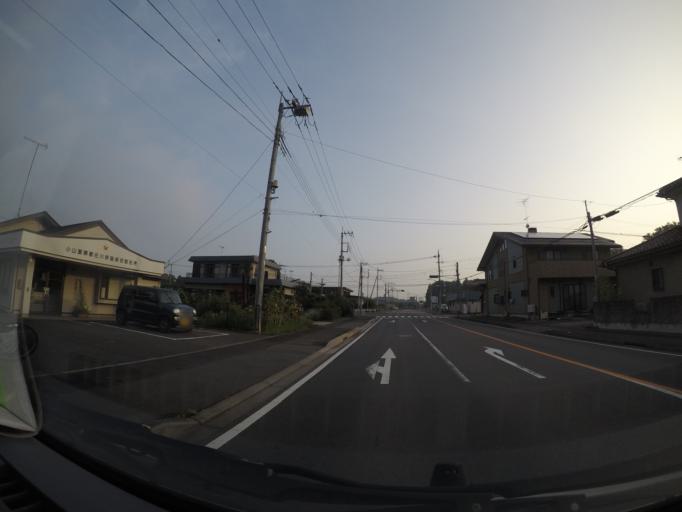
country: JP
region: Ibaraki
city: Koga
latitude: 36.2289
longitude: 139.7696
